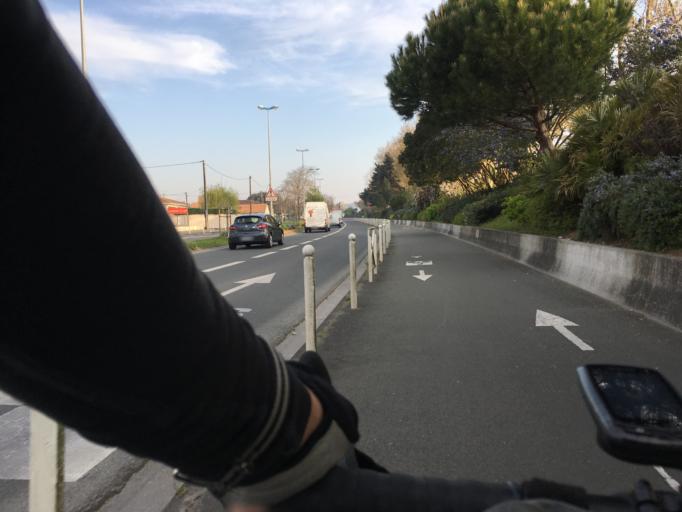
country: FR
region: Poitou-Charentes
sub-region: Departement de la Charente-Maritime
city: La Rochelle
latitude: 46.1750
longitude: -1.1504
